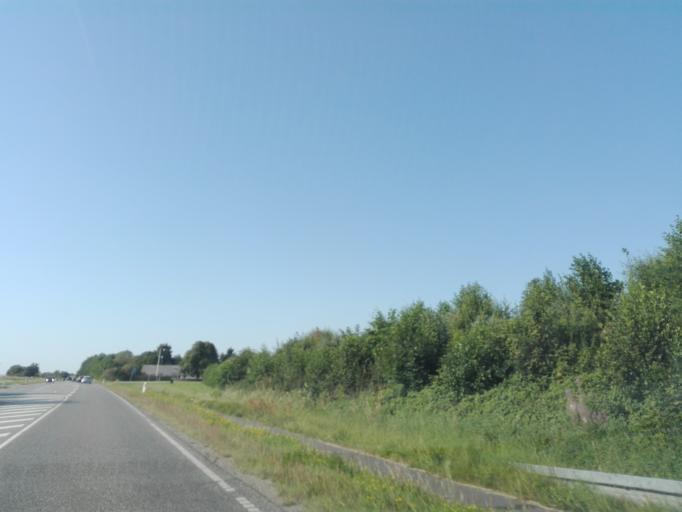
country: DK
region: Central Jutland
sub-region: Odder Kommune
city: Odder
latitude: 55.9225
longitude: 10.2463
